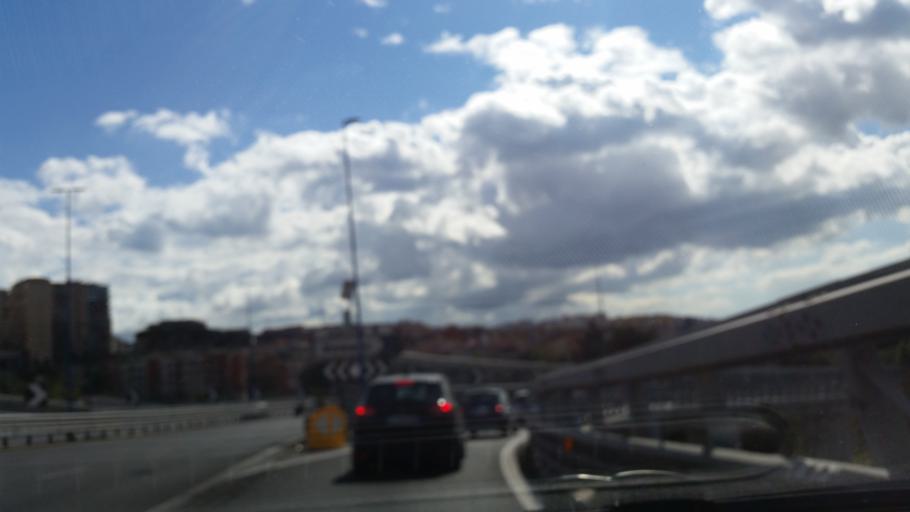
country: IT
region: Campania
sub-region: Provincia di Napoli
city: Napoli
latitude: 40.8456
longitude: 14.2162
